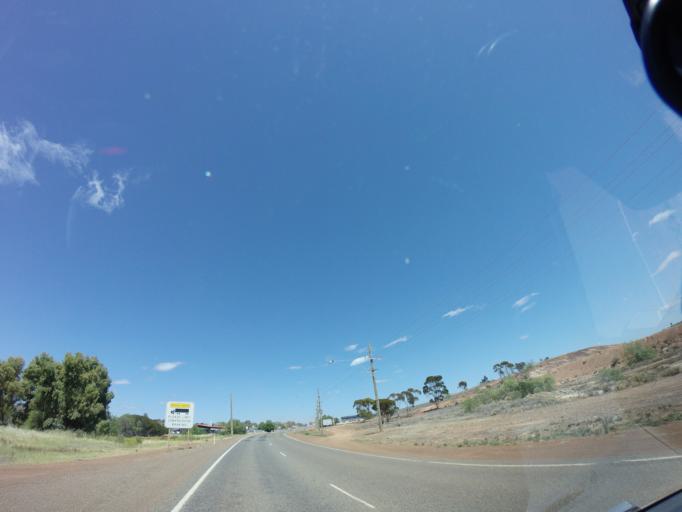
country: AU
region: Western Australia
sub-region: Kalgoorlie/Boulder
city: Boulder
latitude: -30.9546
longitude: 121.1745
